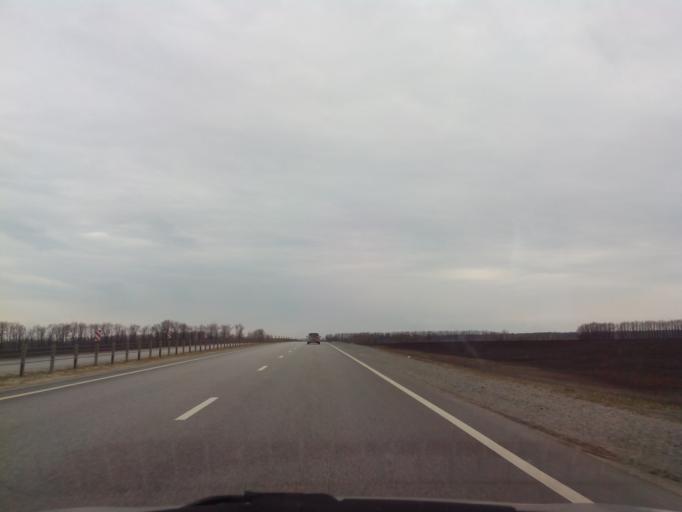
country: RU
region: Tambov
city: Zavoronezhskoye
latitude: 52.8978
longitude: 40.6725
